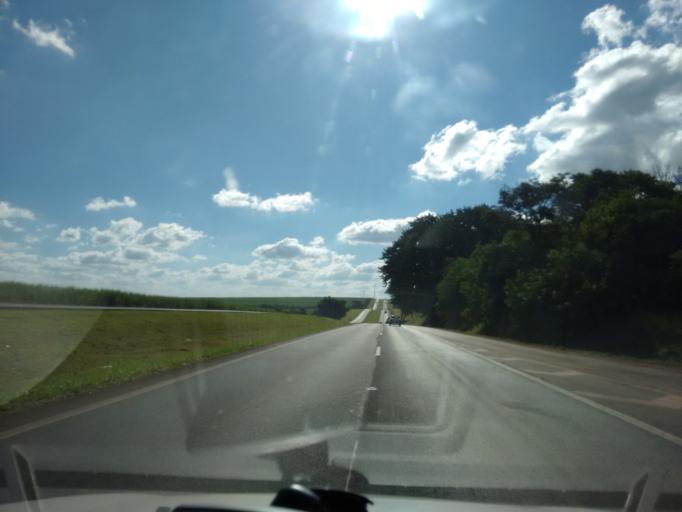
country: BR
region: Sao Paulo
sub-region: Araraquara
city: Araraquara
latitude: -21.8726
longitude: -48.1028
